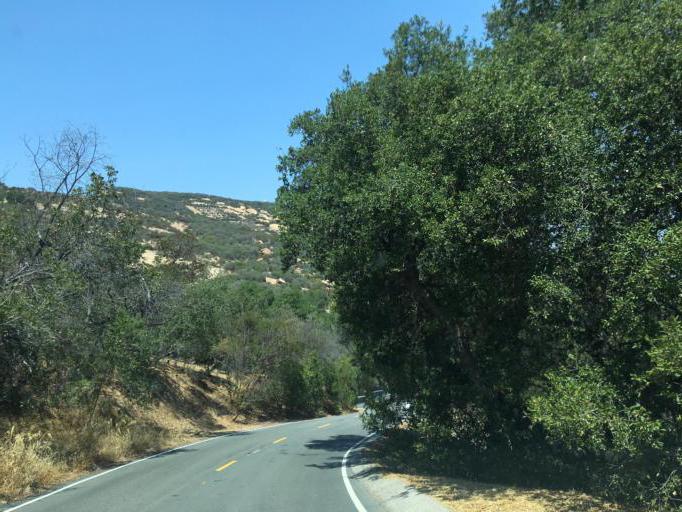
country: US
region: California
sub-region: Los Angeles County
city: Topanga
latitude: 34.0727
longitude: -118.6073
